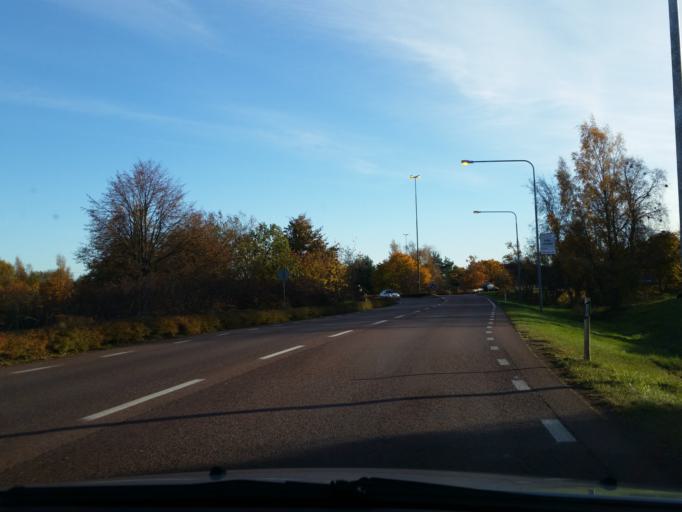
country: AX
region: Mariehamns stad
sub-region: Mariehamn
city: Mariehamn
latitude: 60.1160
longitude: 19.9387
